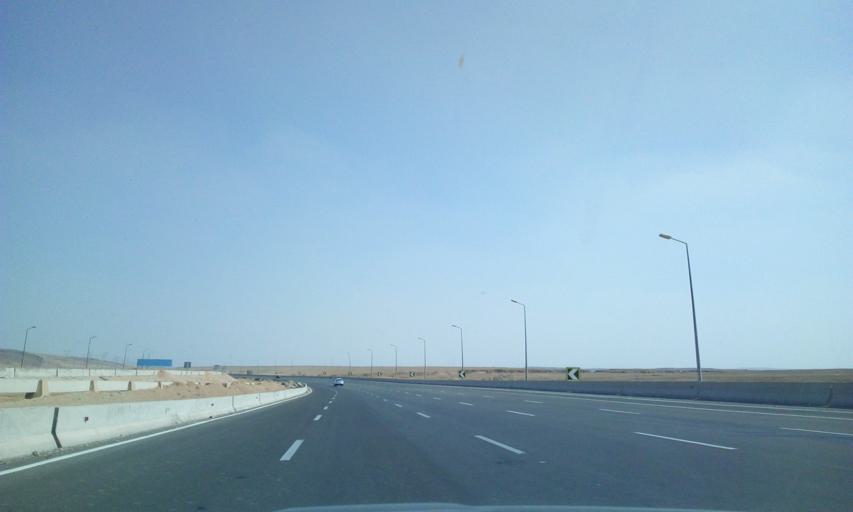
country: EG
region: As Suways
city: Ain Sukhna
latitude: 29.8307
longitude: 31.8816
